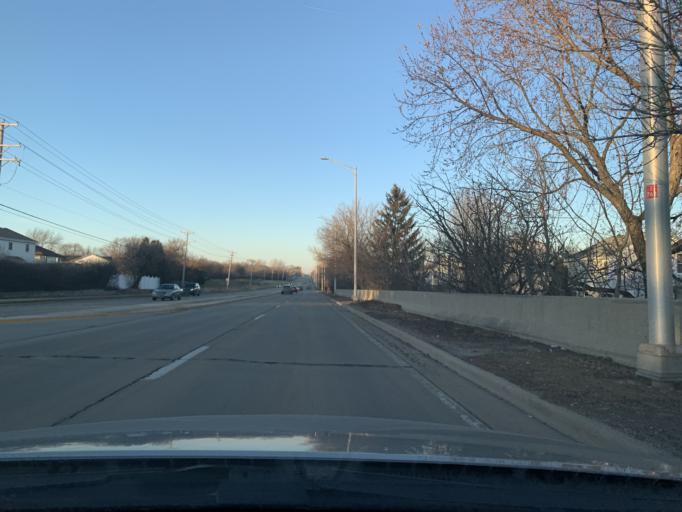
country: US
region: Illinois
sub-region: DuPage County
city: Roselle
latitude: 42.0080
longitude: -88.0604
